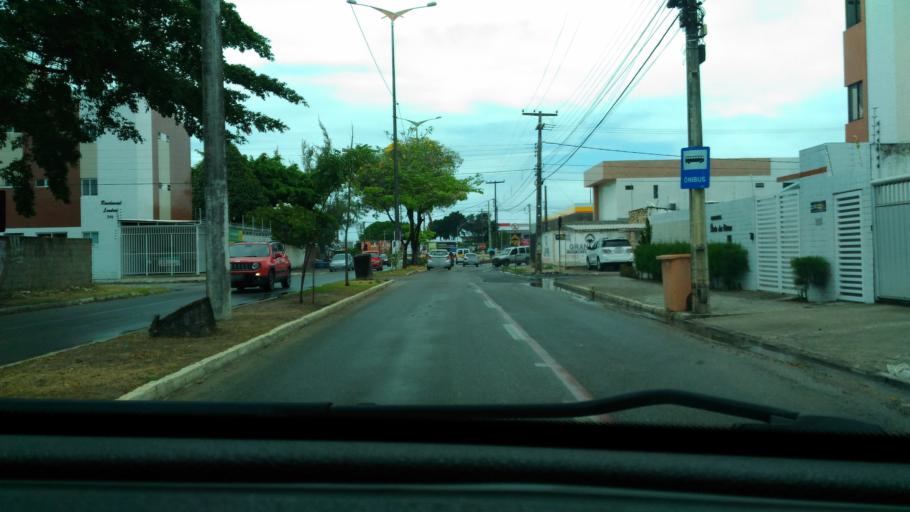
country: BR
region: Paraiba
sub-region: Joao Pessoa
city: Joao Pessoa
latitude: -7.1591
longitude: -34.8190
